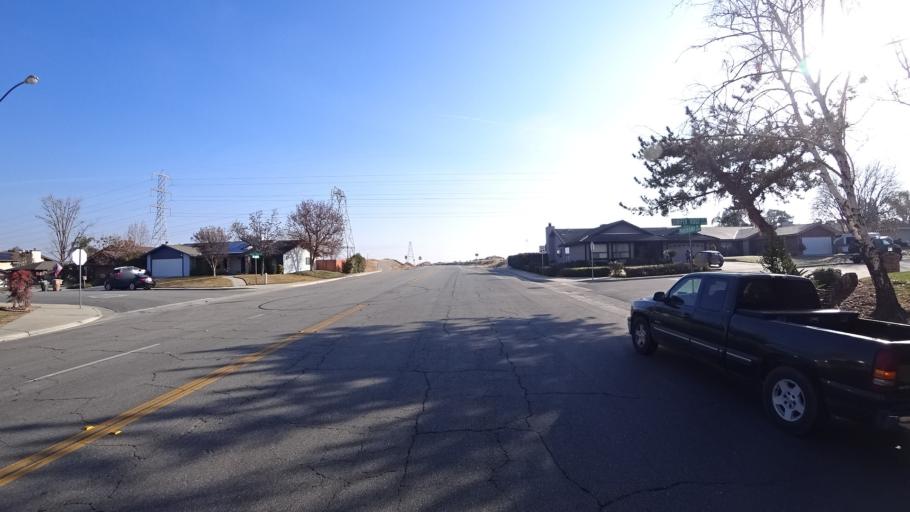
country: US
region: California
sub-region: Kern County
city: Oildale
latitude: 35.4028
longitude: -118.9239
